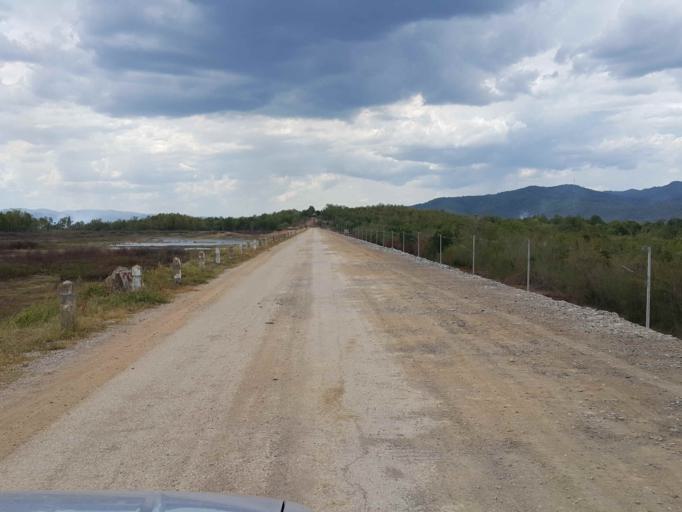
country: TH
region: Sukhothai
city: Thung Saliam
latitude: 17.3191
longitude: 99.4237
